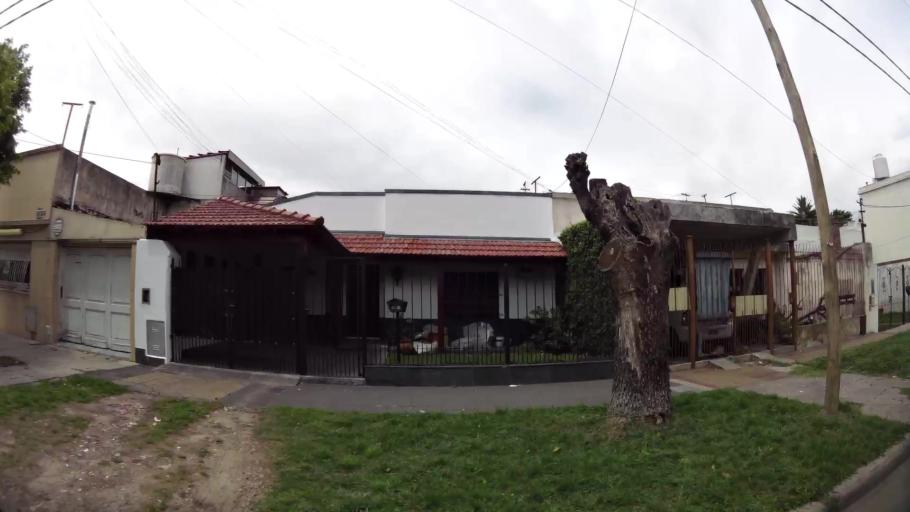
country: AR
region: Buenos Aires
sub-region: Partido de Avellaneda
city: Avellaneda
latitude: -34.6799
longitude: -58.3712
